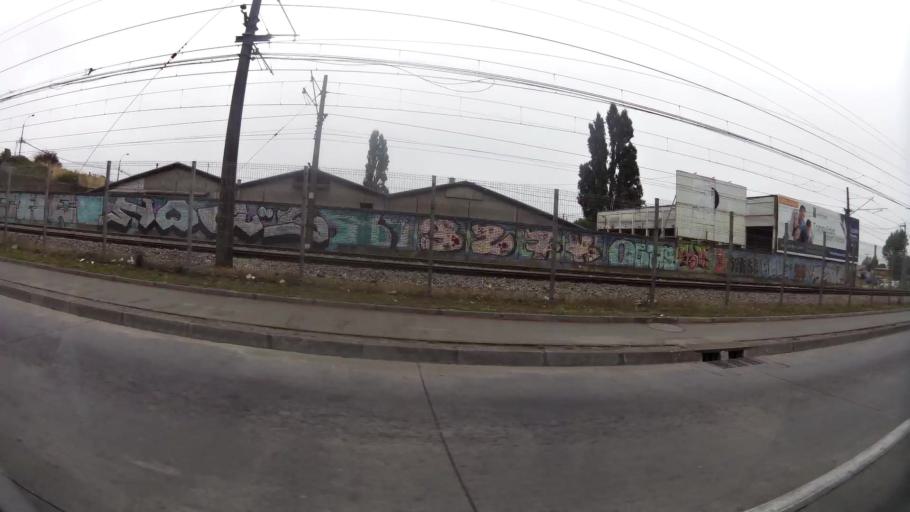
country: CL
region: Biobio
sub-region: Provincia de Concepcion
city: Concepcion
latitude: -36.8350
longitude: -73.0569
